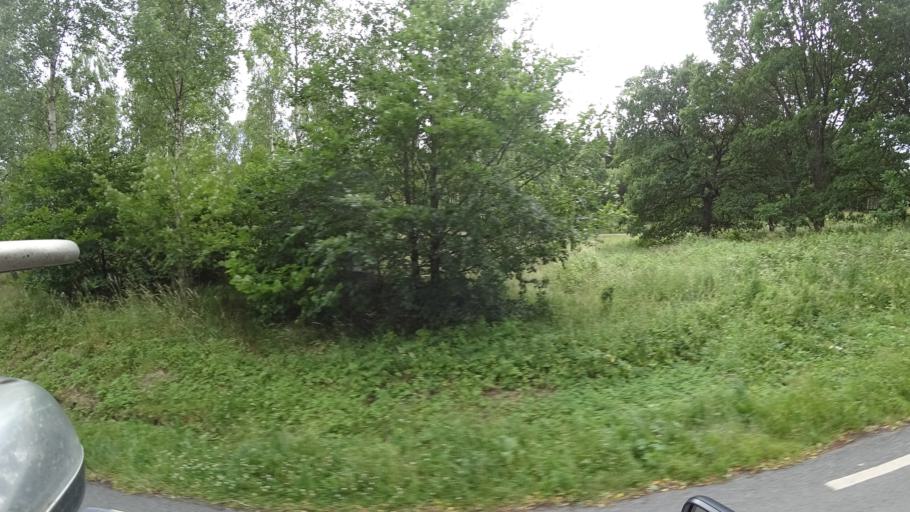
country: SE
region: Skane
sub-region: Kristianstads Kommun
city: Degeberga
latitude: 55.7175
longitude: 13.9897
